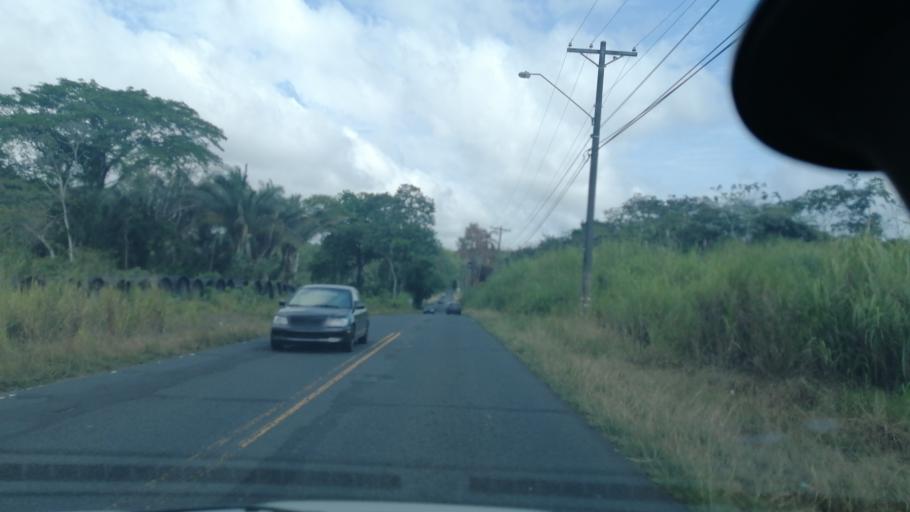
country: PA
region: Panama
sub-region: Distrito de Panama
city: Paraiso
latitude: 9.0518
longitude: -79.6374
